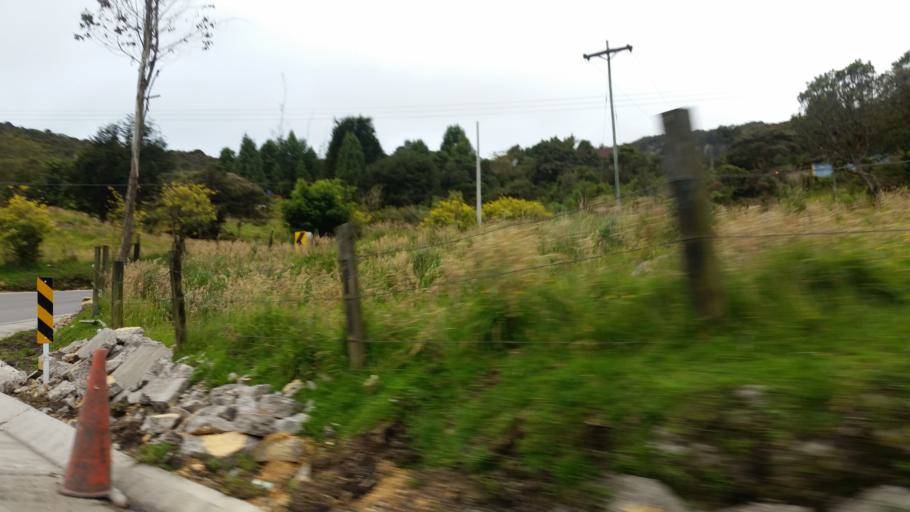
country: CO
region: Cundinamarca
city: Choachi
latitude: 4.5641
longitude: -73.9706
